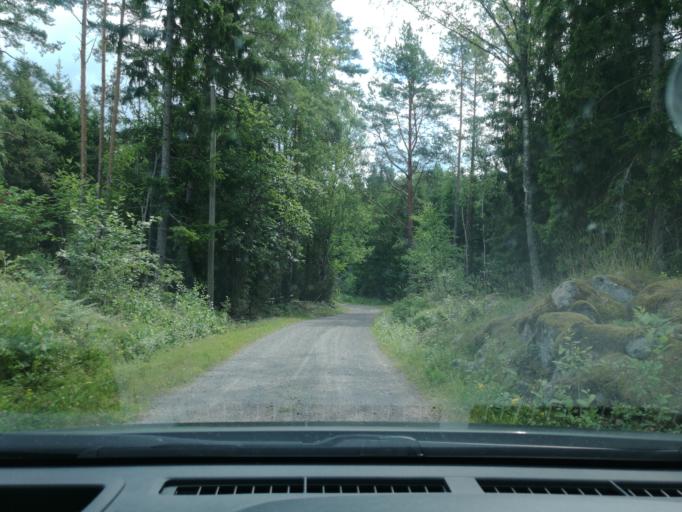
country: SE
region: Stockholm
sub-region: Sigtuna Kommun
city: Marsta
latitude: 59.6666
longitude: 17.9054
